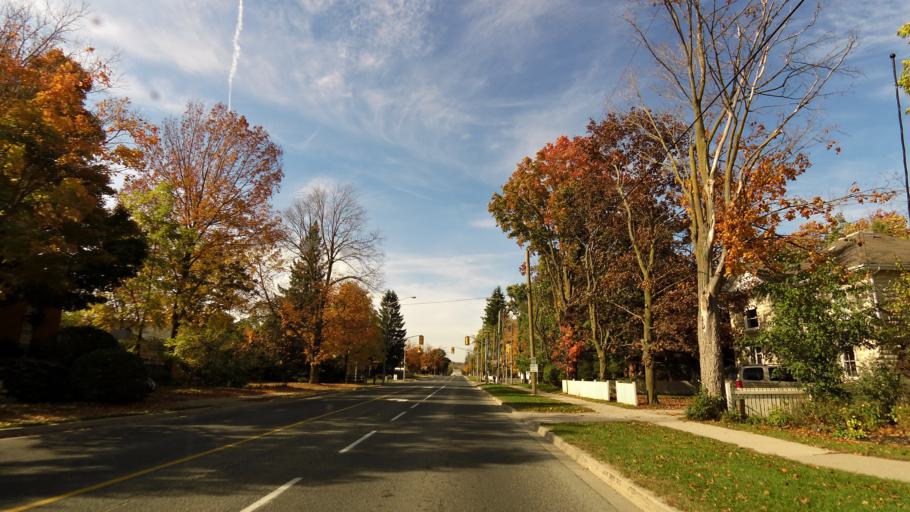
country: CA
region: Ontario
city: Orangeville
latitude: 43.7744
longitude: -80.0695
